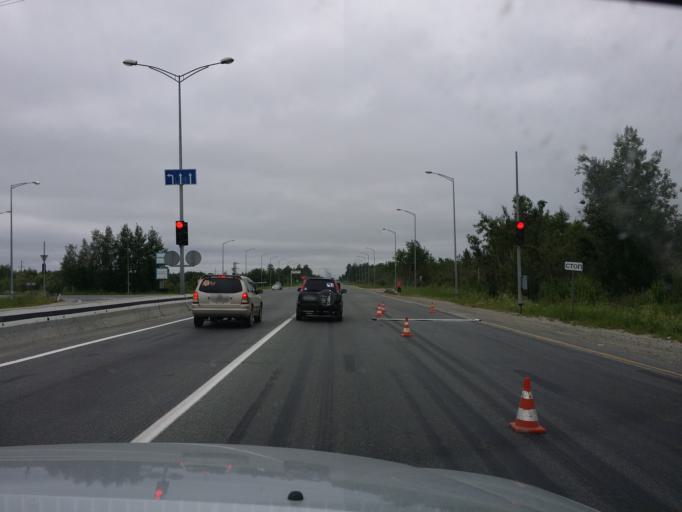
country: RU
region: Khanty-Mansiyskiy Avtonomnyy Okrug
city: Nizhnevartovsk
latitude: 60.9913
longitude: 76.4364
